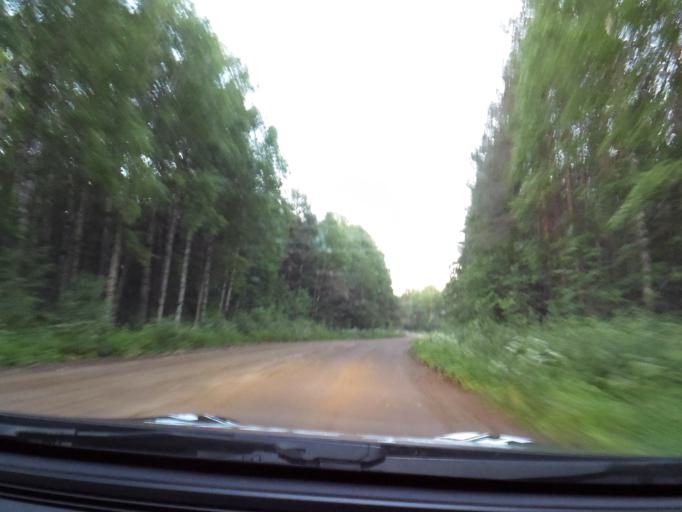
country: RU
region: Leningrad
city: Voznesen'ye
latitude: 60.8543
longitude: 35.8847
